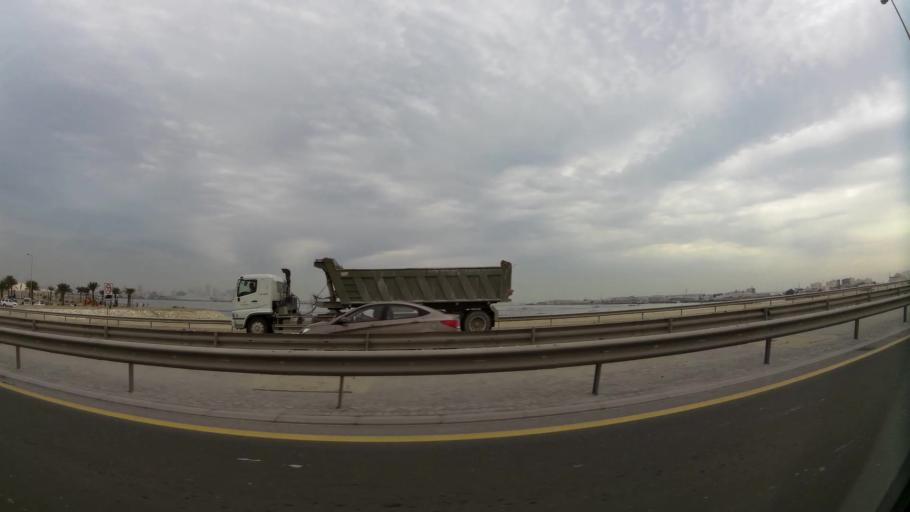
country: BH
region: Northern
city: Sitrah
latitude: 26.1768
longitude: 50.5944
